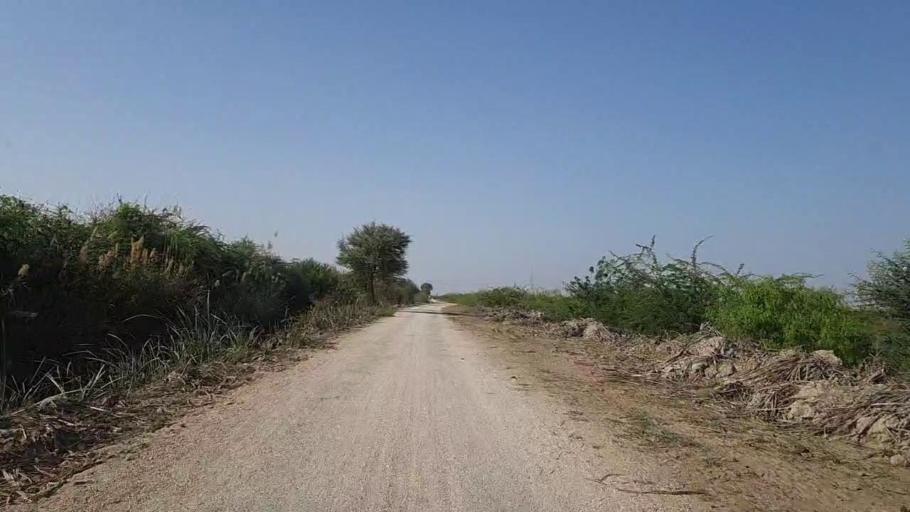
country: PK
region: Sindh
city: Kotri
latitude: 25.1434
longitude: 68.2658
